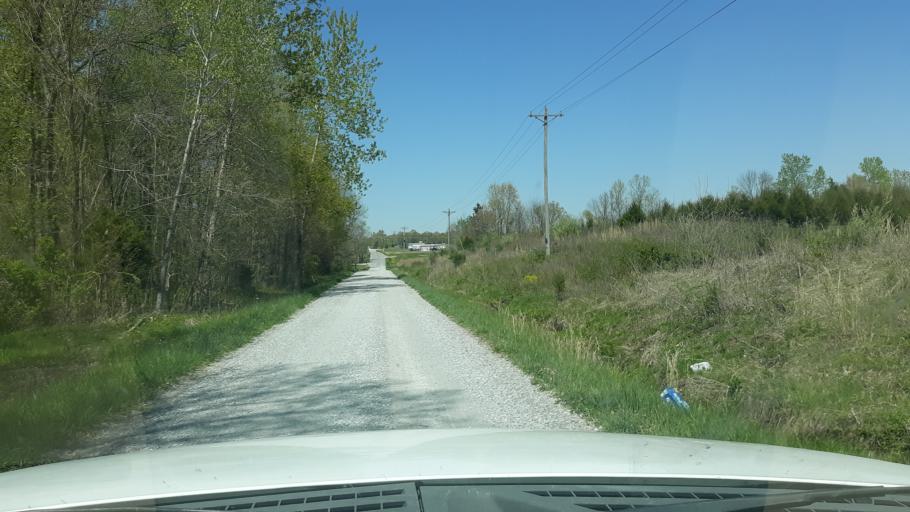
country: US
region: Illinois
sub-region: Saline County
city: Harrisburg
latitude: 37.8721
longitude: -88.6422
